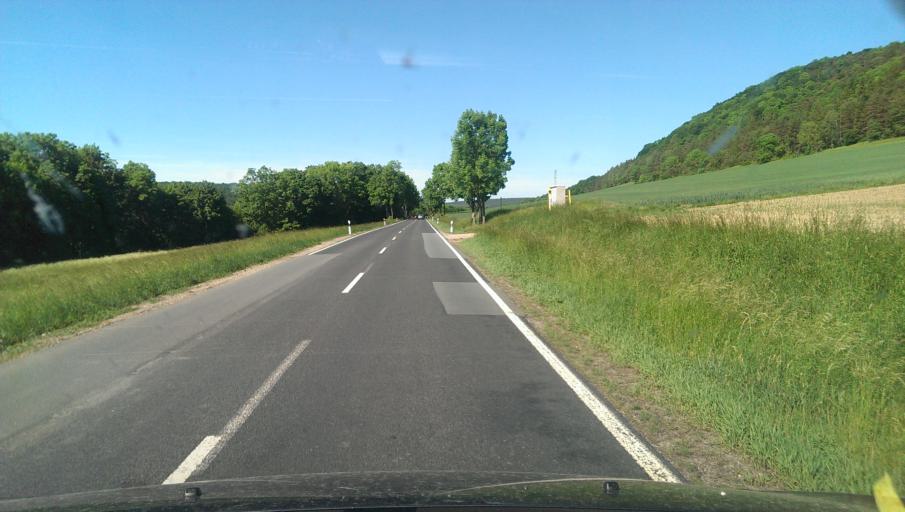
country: DE
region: Thuringia
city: Barchfeld
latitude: 50.8333
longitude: 11.1825
